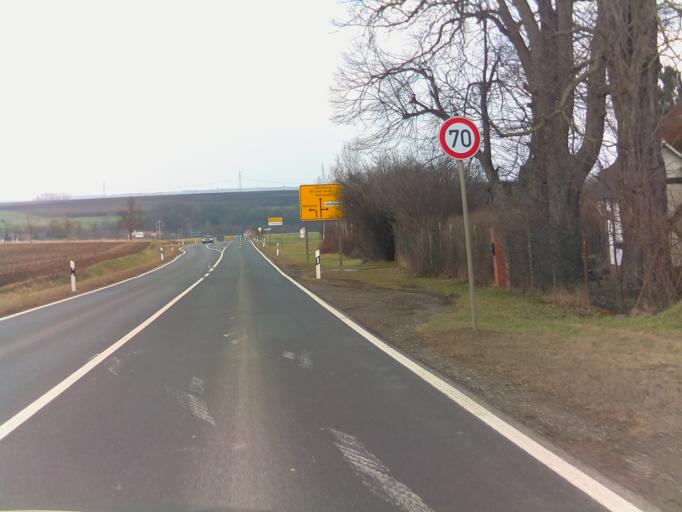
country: DE
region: Thuringia
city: Mattstedt
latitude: 51.0496
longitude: 11.5158
